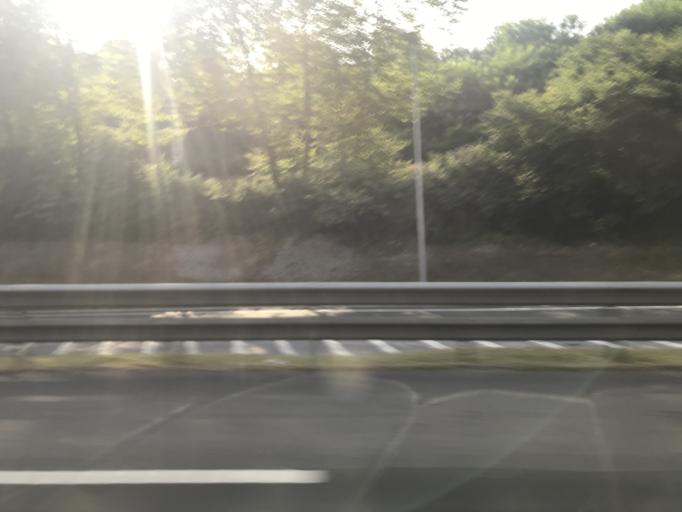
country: ES
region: Basque Country
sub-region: Provincia de Guipuzcoa
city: Aduna
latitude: 43.2034
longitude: -2.0364
